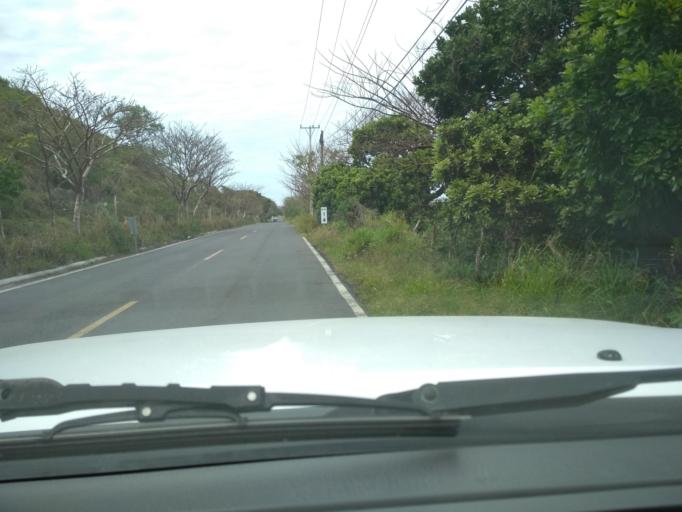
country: MX
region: Veracruz
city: Anton Lizardo
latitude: 19.0402
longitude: -95.9856
